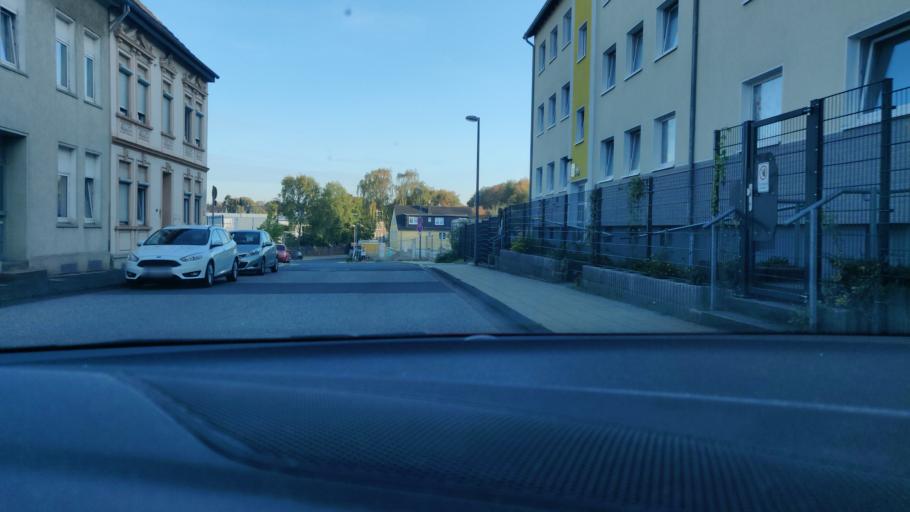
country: DE
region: North Rhine-Westphalia
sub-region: Regierungsbezirk Dusseldorf
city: Velbert
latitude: 51.3471
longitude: 7.0491
